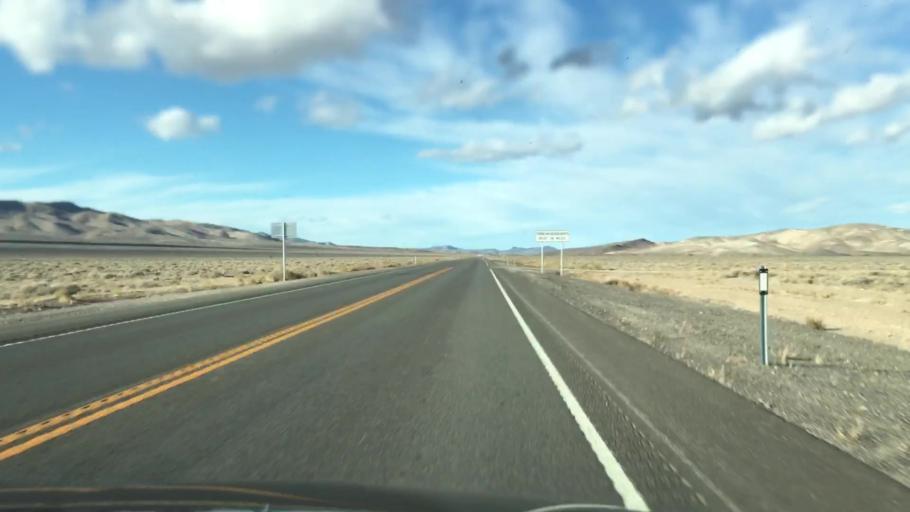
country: US
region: Nevada
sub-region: Esmeralda County
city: Goldfield
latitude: 37.5057
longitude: -117.1859
